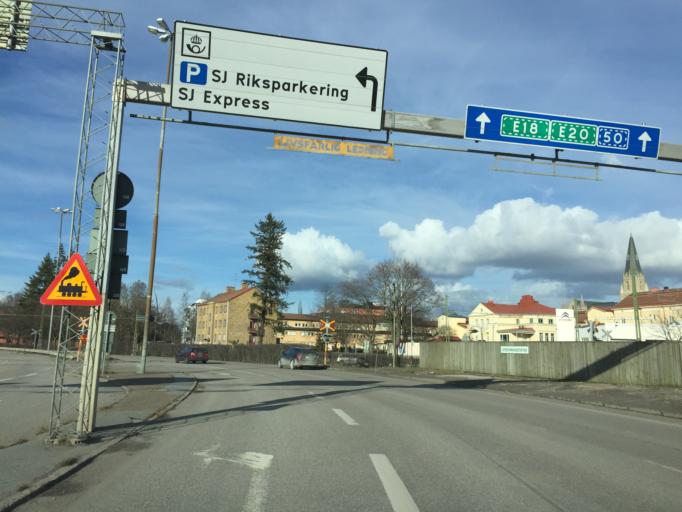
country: SE
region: OErebro
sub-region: Orebro Kommun
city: Orebro
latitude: 59.2759
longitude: 15.2099
